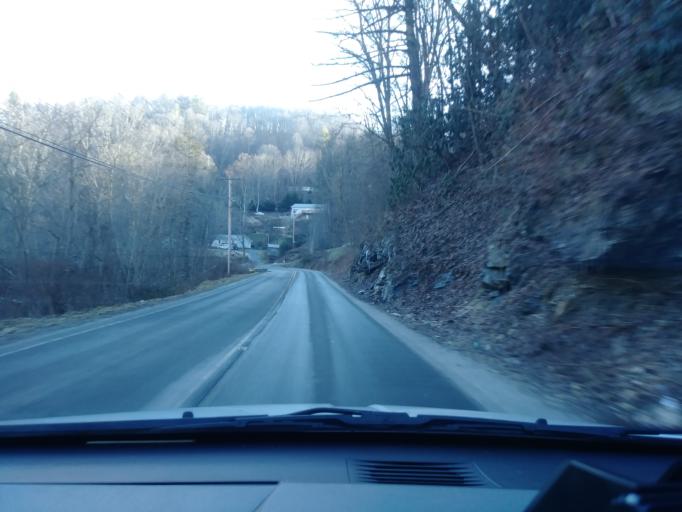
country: US
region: North Carolina
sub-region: Avery County
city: Banner Elk
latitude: 36.1693
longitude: -81.9499
